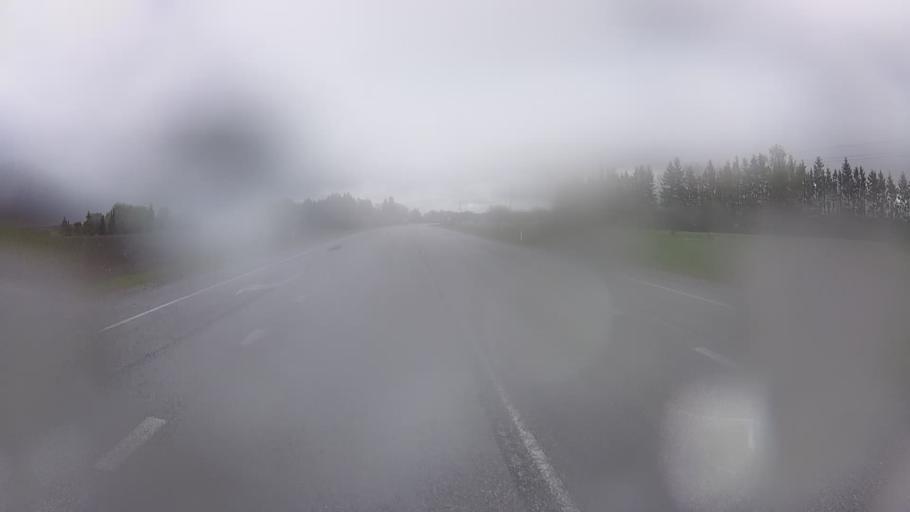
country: EE
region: Hiiumaa
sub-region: Kaerdla linn
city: Kardla
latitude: 58.8350
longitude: 22.7896
